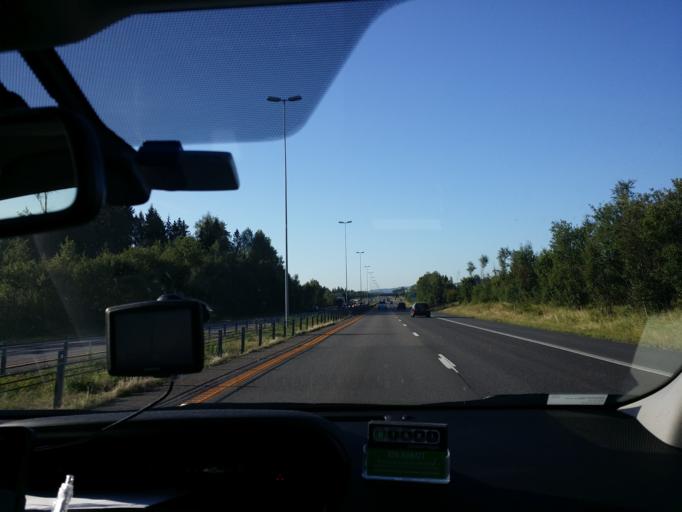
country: NO
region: Akershus
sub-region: Ullensaker
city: Klofta
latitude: 60.0874
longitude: 11.1474
